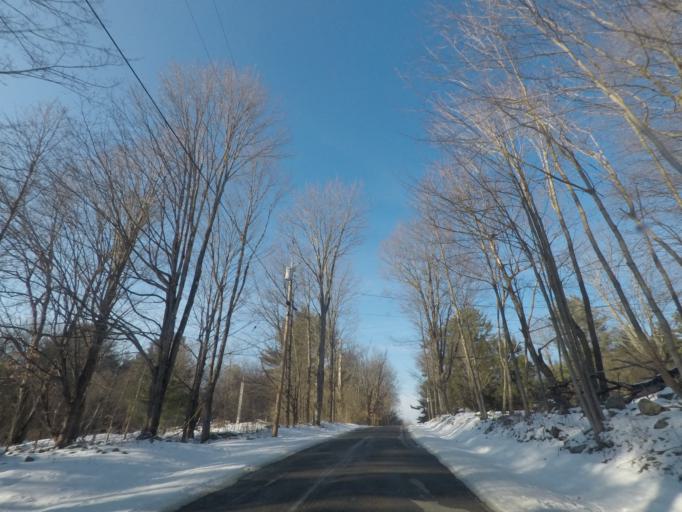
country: US
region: New York
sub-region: Rensselaer County
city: Nassau
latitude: 42.4992
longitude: -73.5038
